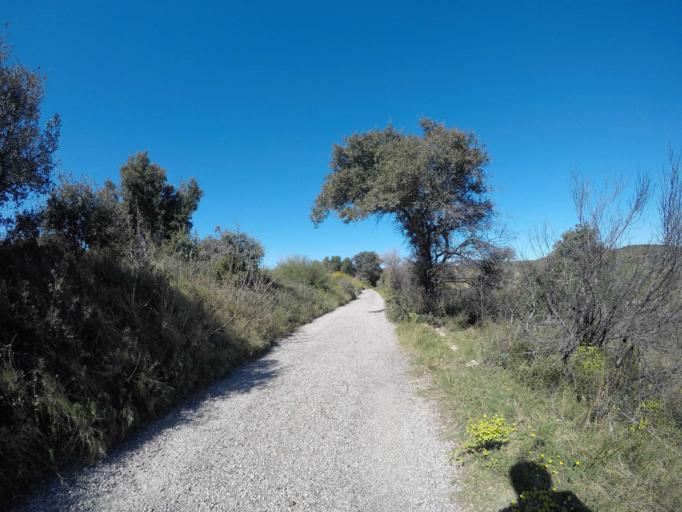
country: FR
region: Languedoc-Roussillon
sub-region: Departement des Pyrenees-Orientales
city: Millas
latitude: 42.7068
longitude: 2.6711
